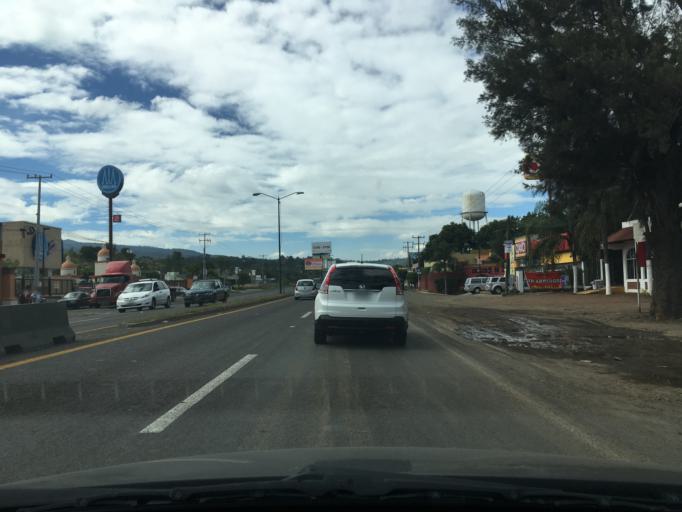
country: MX
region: Michoacan
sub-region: Morelia
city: Morelos
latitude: 19.6691
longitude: -101.2232
